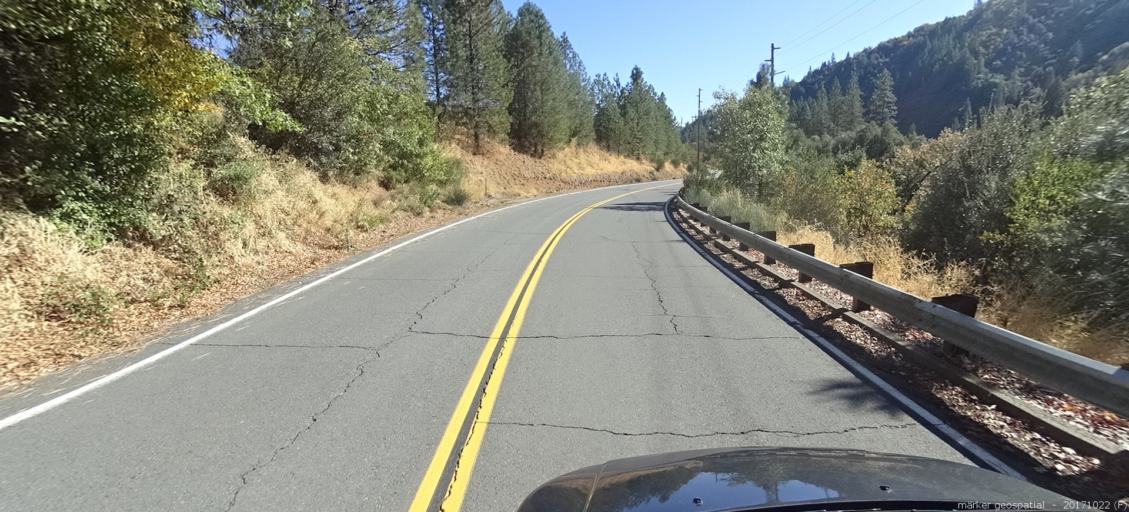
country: US
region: California
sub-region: Shasta County
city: Central Valley (historical)
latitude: 40.9417
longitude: -122.4360
